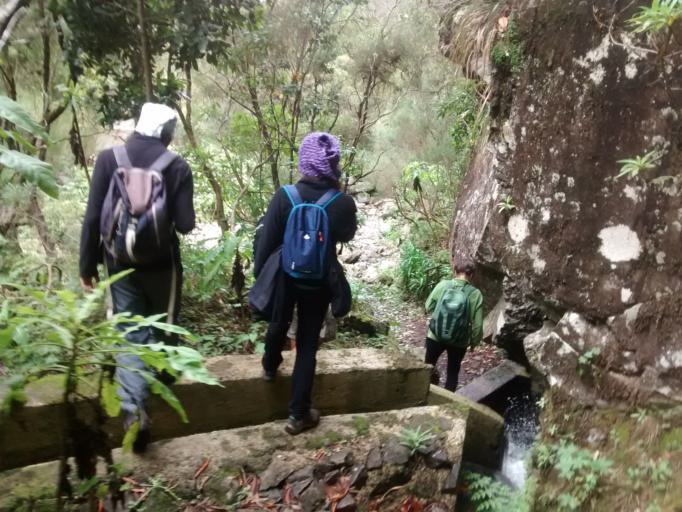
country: PT
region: Madeira
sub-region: Sao Vicente
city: Sao Vicente
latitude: 32.7577
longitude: -17.0477
